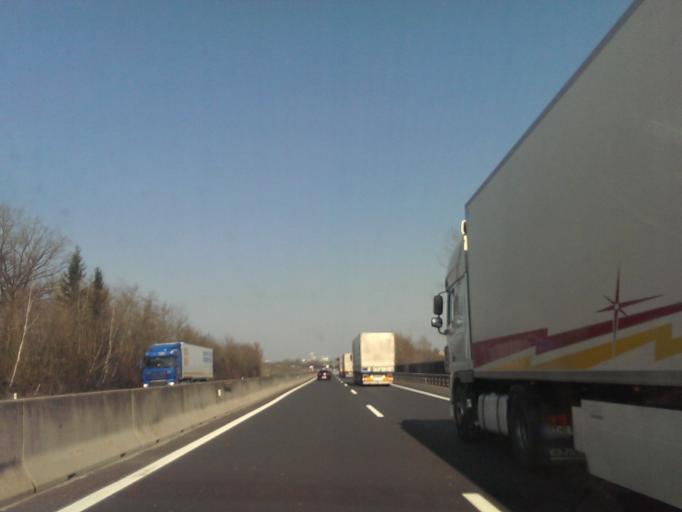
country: AT
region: Upper Austria
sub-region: Politischer Bezirk Scharding
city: Sankt Marienkirchen bei Schaerding
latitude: 48.3808
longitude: 13.4184
